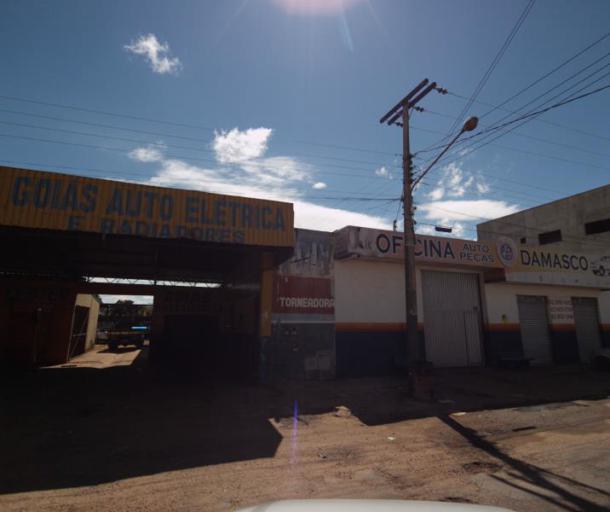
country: BR
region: Goias
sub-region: Uruacu
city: Uruacu
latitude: -14.5223
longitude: -49.1562
